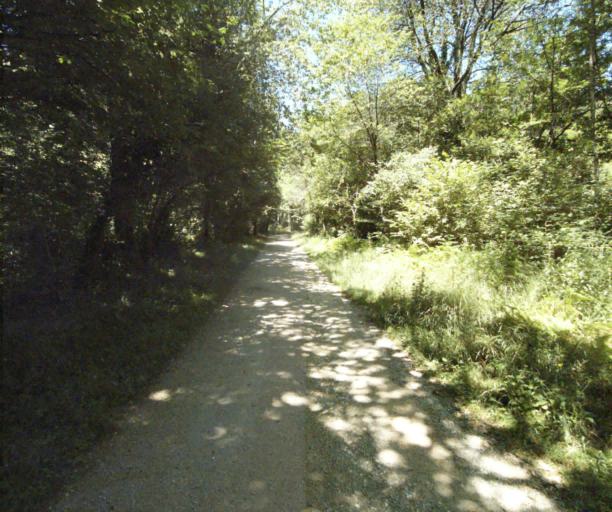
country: FR
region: Midi-Pyrenees
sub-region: Departement du Tarn
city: Dourgne
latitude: 43.4204
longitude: 2.1513
